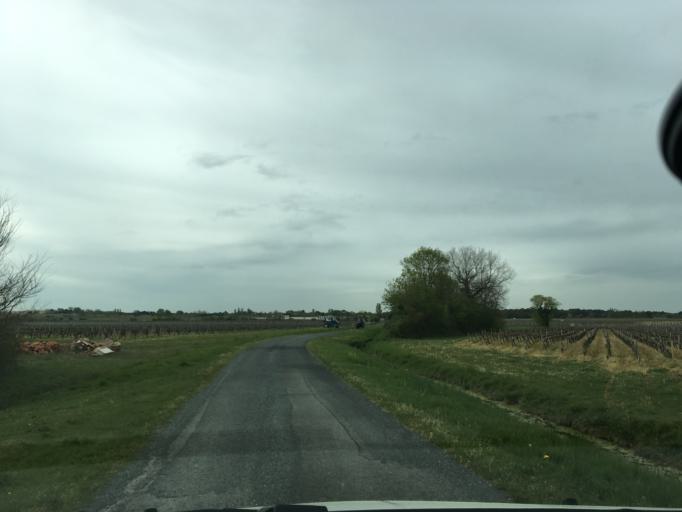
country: FR
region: Aquitaine
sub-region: Departement de la Gironde
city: Lesparre-Medoc
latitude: 45.3230
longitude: -0.8951
